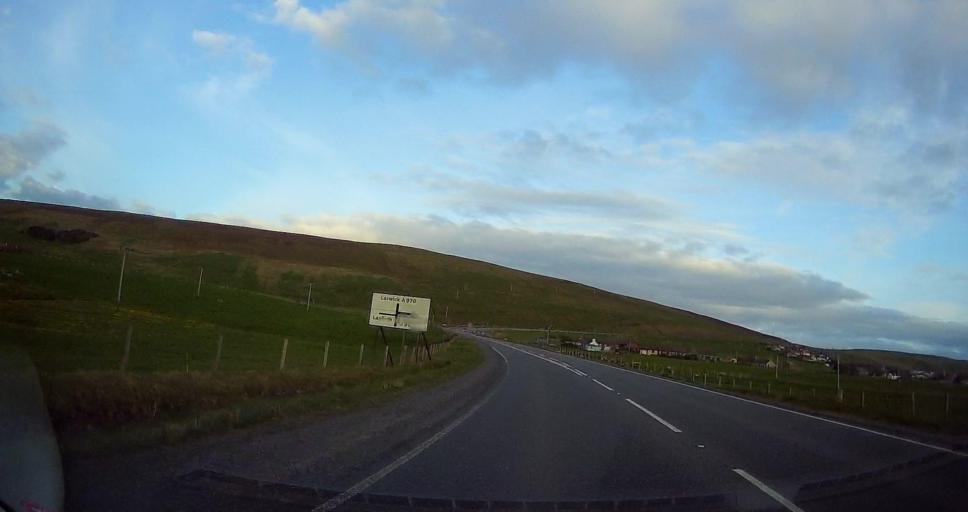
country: GB
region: Scotland
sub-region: Shetland Islands
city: Lerwick
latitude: 60.1880
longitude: -1.2304
